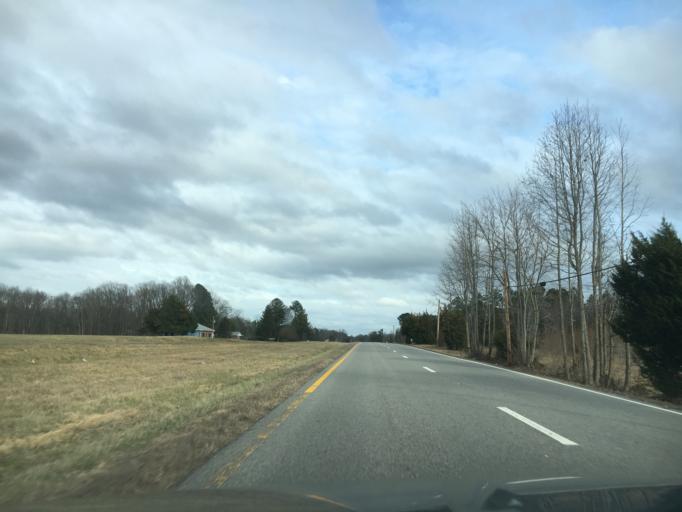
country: US
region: Virginia
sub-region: Prince Edward County
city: Hampden Sydney
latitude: 37.0798
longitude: -78.4347
